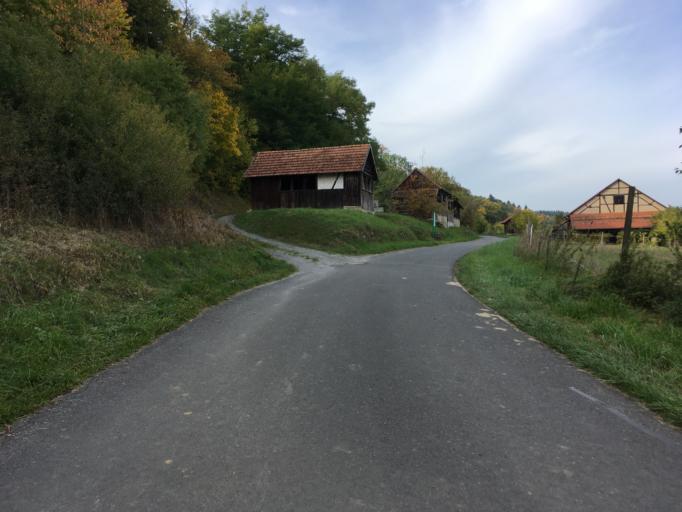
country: DE
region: Baden-Wuerttemberg
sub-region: Karlsruhe Region
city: Rosenberg
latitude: 49.4882
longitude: 9.4512
